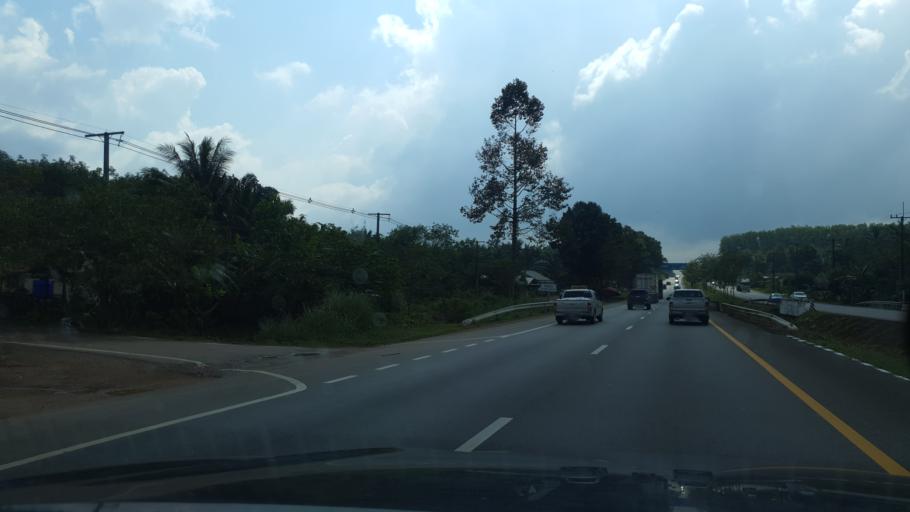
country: TH
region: Chumphon
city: Tha Sae
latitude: 10.7748
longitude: 99.1928
